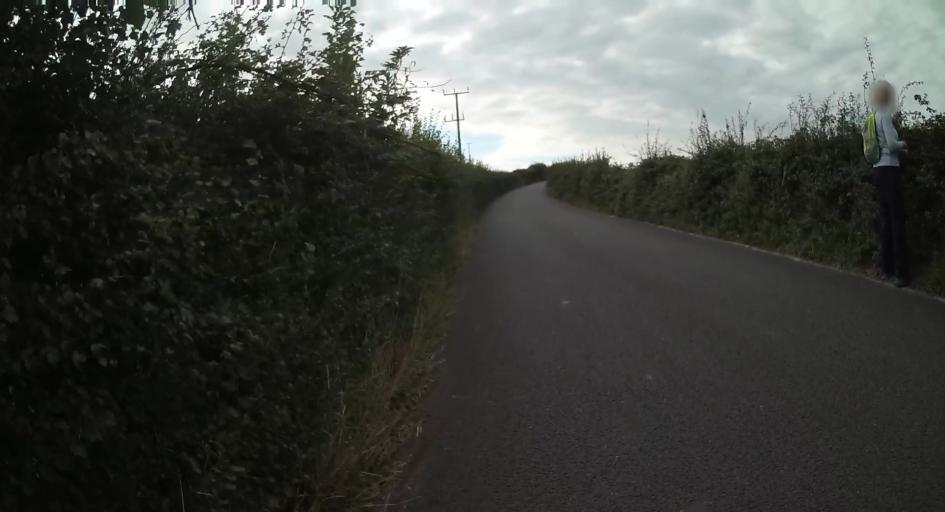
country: GB
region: England
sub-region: Isle of Wight
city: Totland
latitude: 50.6704
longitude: -1.5500
